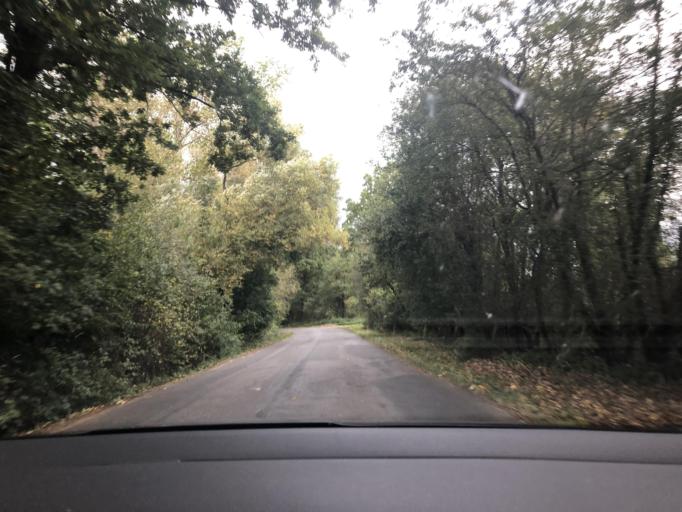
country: CZ
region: Pardubicky
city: Chvaletice
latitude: 50.0500
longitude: 15.4276
